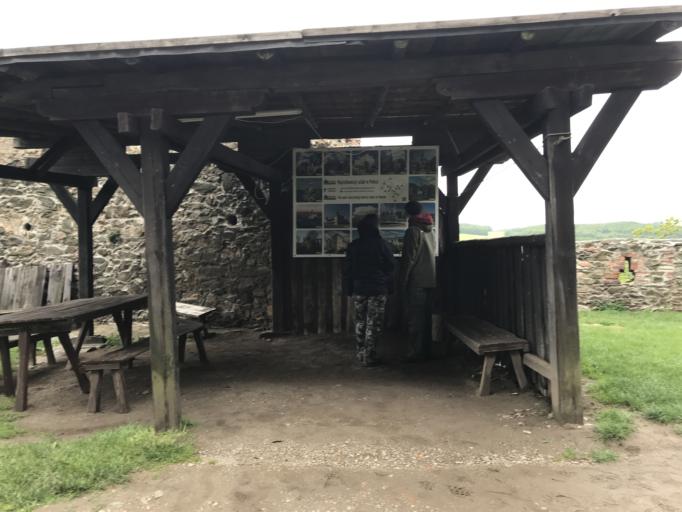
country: PL
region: Lower Silesian Voivodeship
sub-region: Powiat jaworski
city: Bolkow
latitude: 50.9217
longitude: 16.0975
